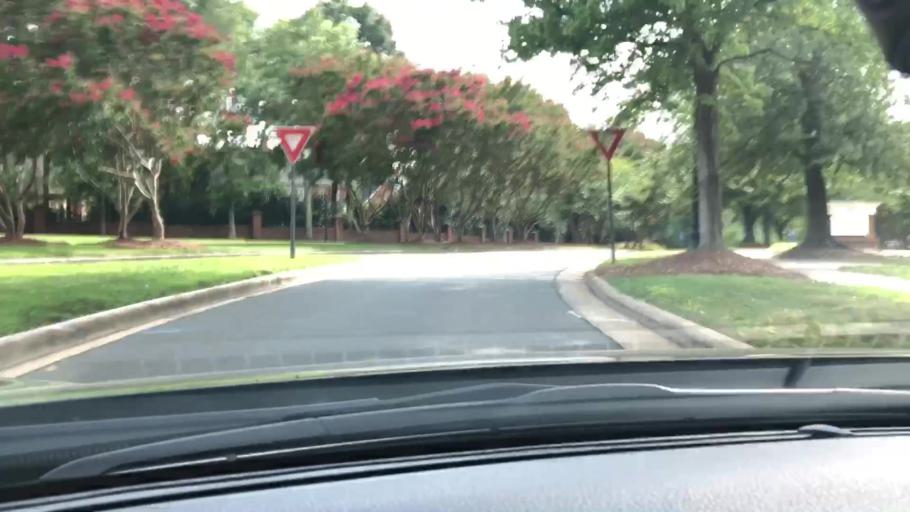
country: US
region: North Carolina
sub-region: Mecklenburg County
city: Charlotte
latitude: 35.1516
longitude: -80.8222
